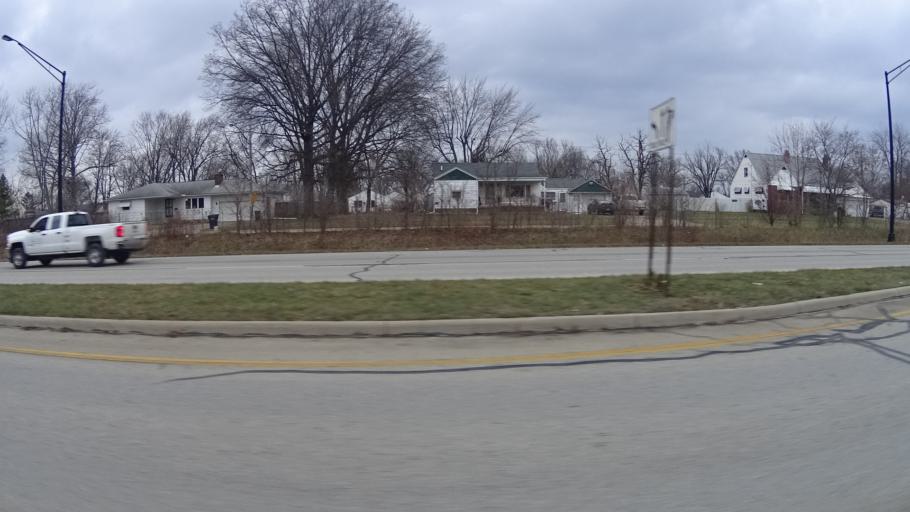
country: US
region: Ohio
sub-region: Lorain County
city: Elyria
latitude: 41.3827
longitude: -82.1089
